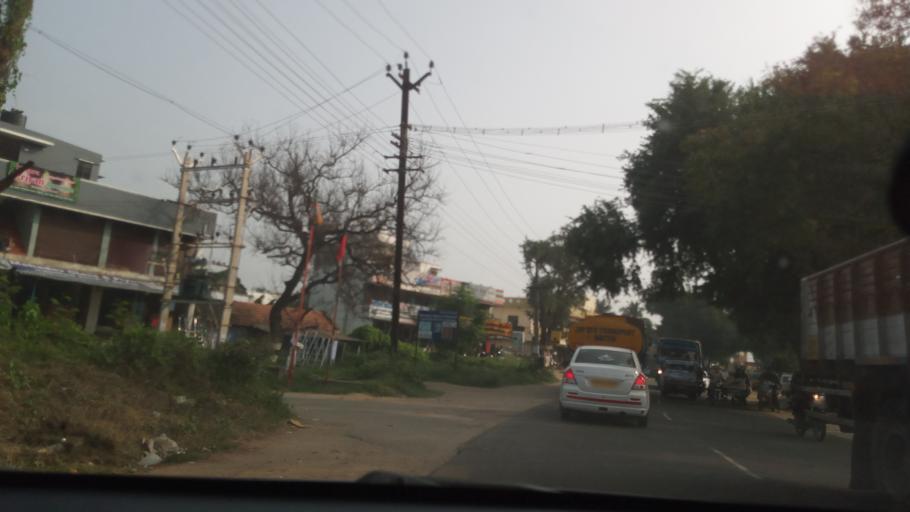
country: IN
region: Tamil Nadu
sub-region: Coimbatore
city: Periyanayakkanpalaiyam
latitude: 11.1419
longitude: 77.0374
